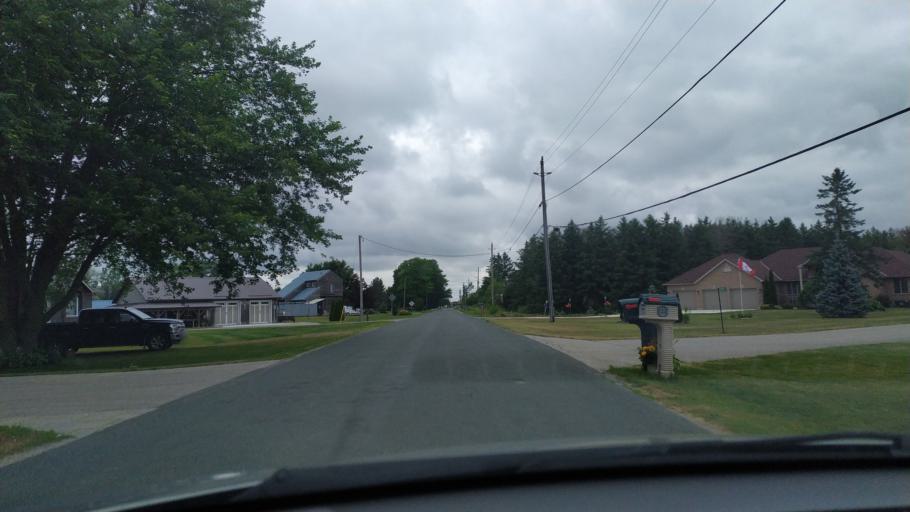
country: CA
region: Ontario
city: Stratford
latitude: 43.3674
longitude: -80.9316
